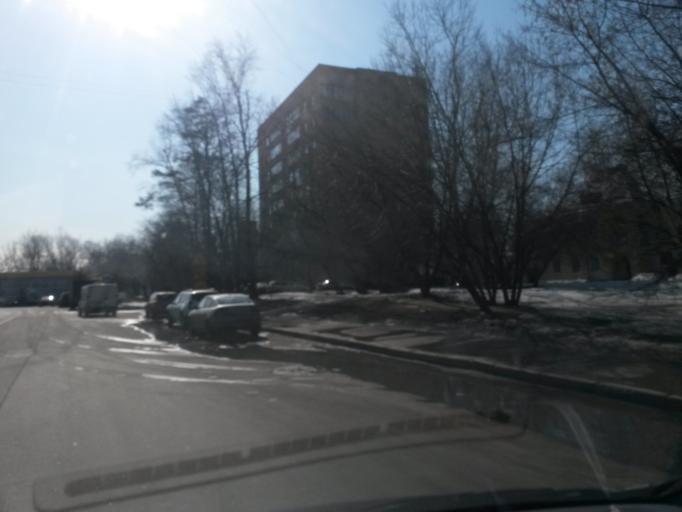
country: RU
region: Moskovskaya
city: Shcherbinka
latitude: 55.5402
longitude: 37.5731
